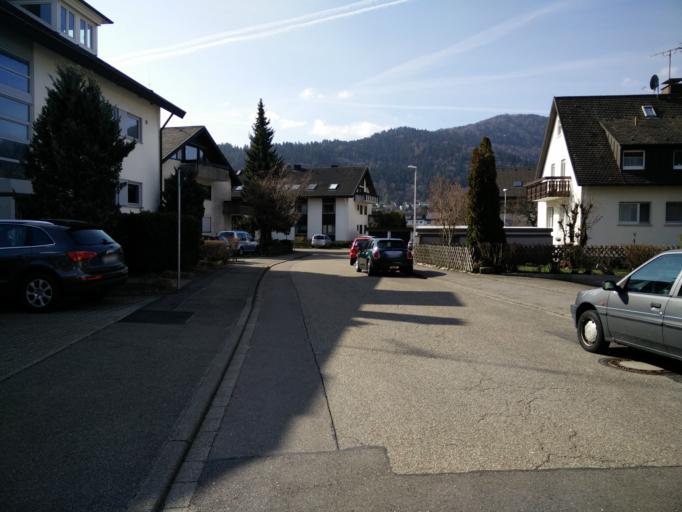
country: DE
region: Baden-Wuerttemberg
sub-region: Freiburg Region
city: Kirchzarten
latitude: 47.9839
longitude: 7.9073
